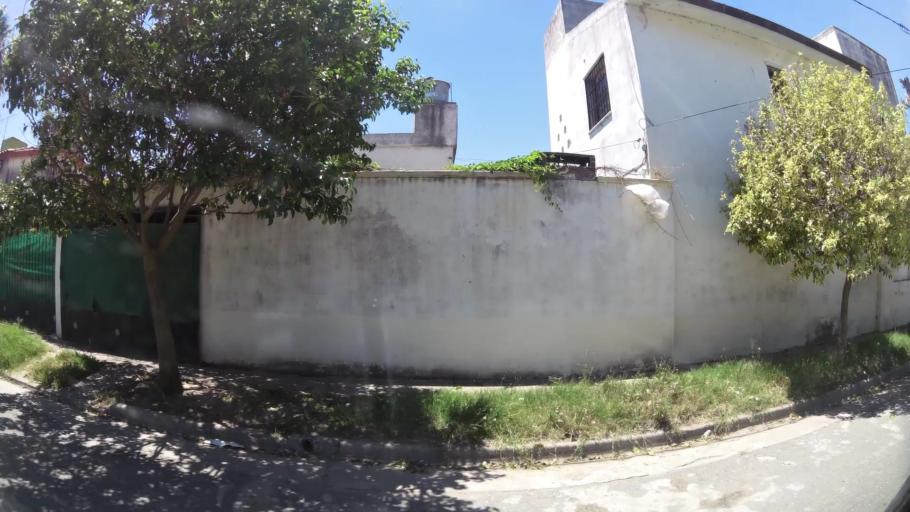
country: AR
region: Cordoba
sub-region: Departamento de Capital
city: Cordoba
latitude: -31.3773
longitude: -64.1336
